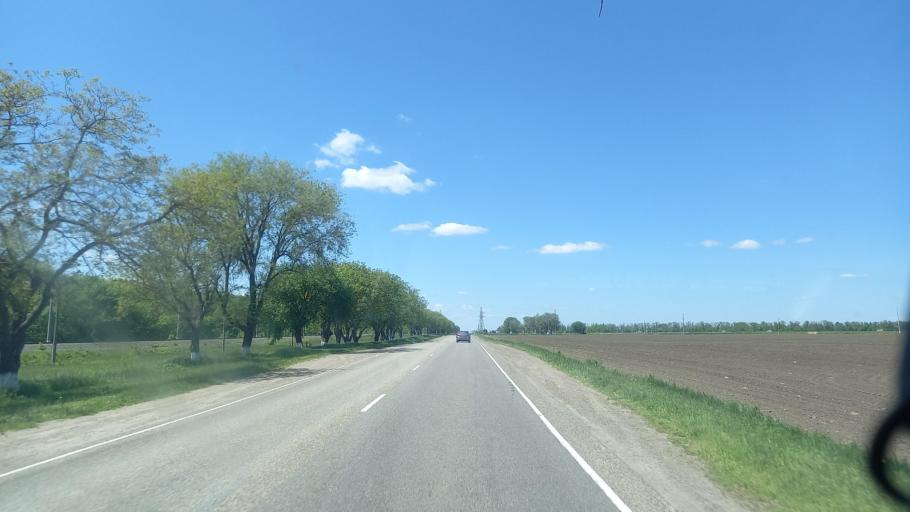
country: RU
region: Krasnodarskiy
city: Tbilisskaya
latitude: 45.3661
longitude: 40.1365
